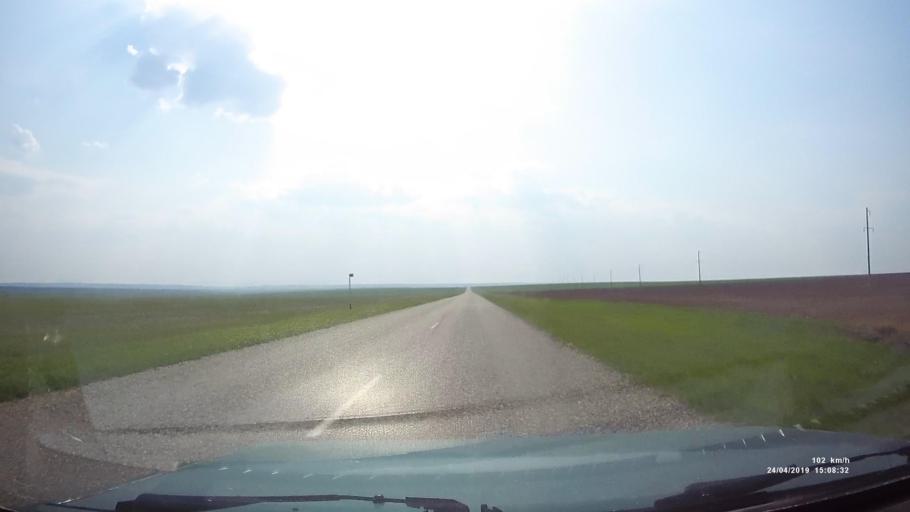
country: RU
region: Rostov
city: Remontnoye
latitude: 46.5593
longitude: 43.3809
